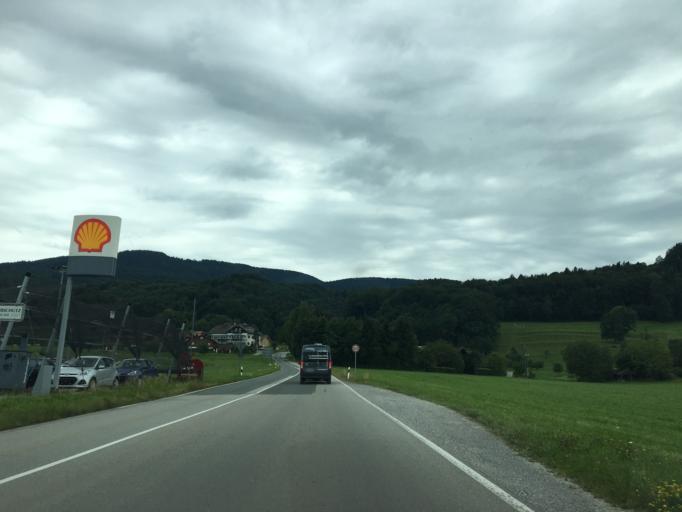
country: DE
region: Bavaria
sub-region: Upper Bavaria
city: Bad Feilnbach
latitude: 47.7785
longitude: 12.0006
